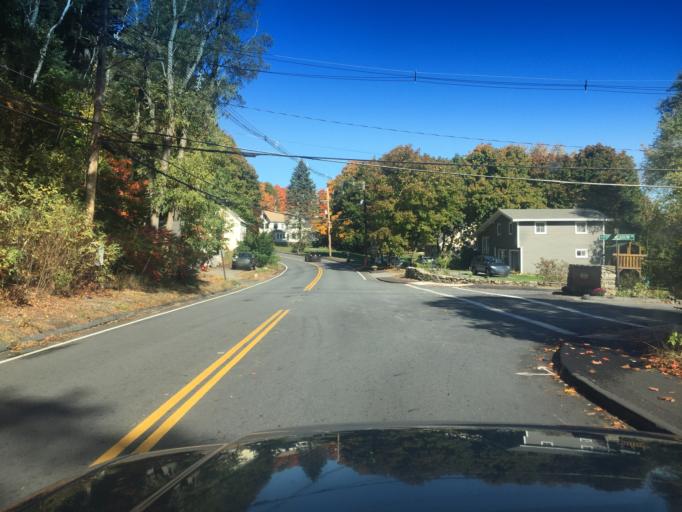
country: US
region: Massachusetts
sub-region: Middlesex County
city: Hudson
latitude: 42.3793
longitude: -71.5500
